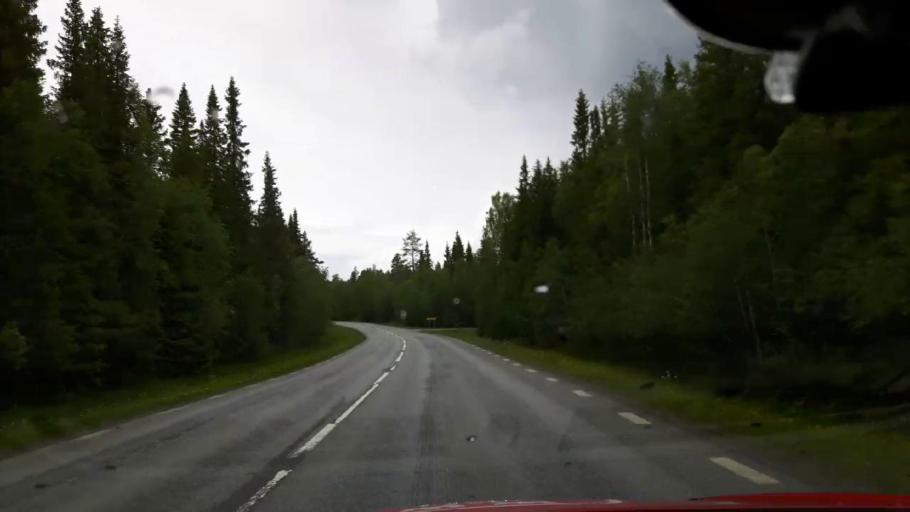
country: SE
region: Jaemtland
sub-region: Krokoms Kommun
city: Krokom
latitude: 63.4320
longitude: 14.2083
